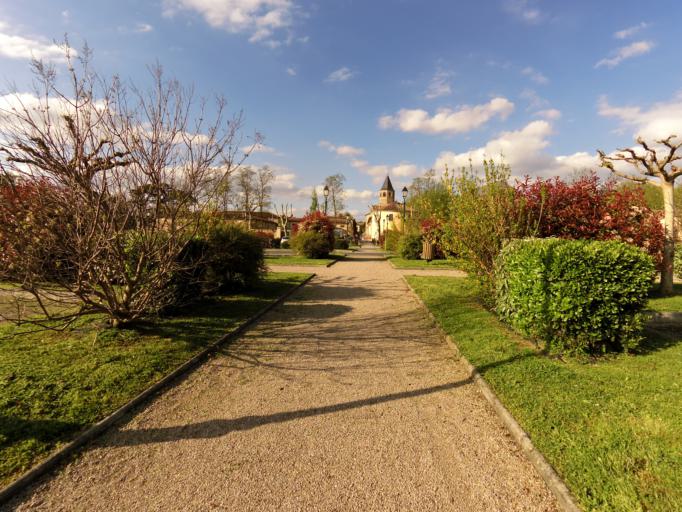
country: FR
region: Midi-Pyrenees
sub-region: Departement du Tarn
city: Soreze
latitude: 43.4502
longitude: 2.0662
